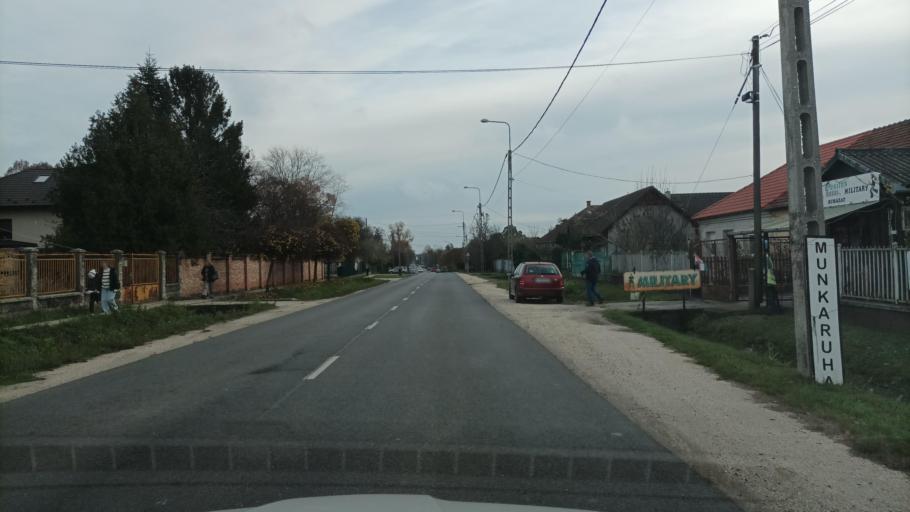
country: HU
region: Pest
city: Ocsa
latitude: 47.2982
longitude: 19.2221
